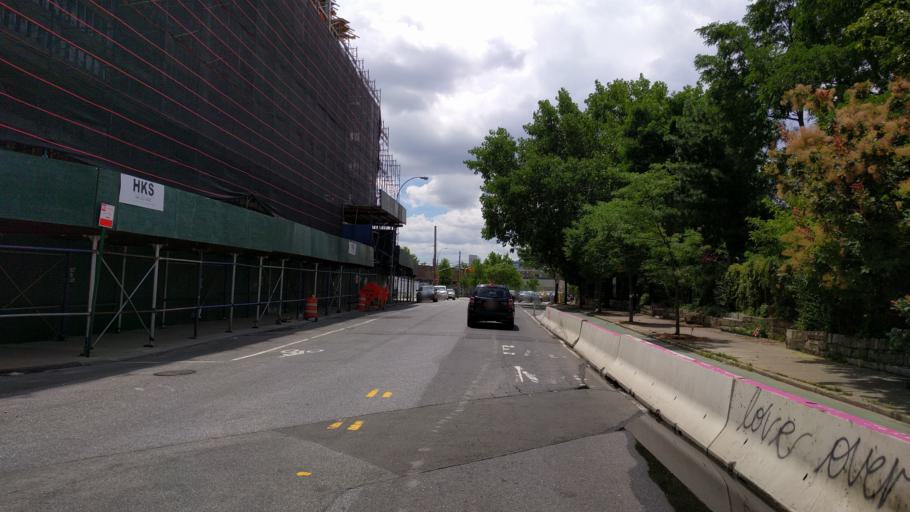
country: US
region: New York
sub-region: Queens County
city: Long Island City
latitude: 40.7687
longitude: -73.9358
